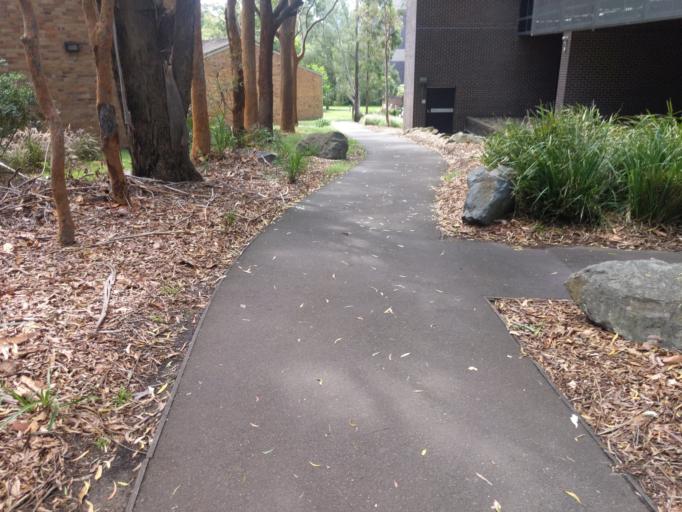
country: AU
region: New South Wales
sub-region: Ryde
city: Macquarie Park
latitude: -33.7762
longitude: 151.1191
